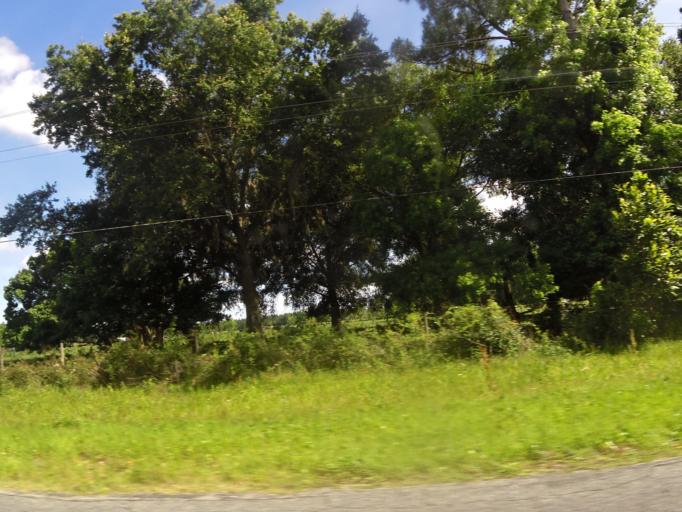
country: US
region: Florida
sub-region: Nassau County
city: Hilliard
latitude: 30.6693
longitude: -81.9114
